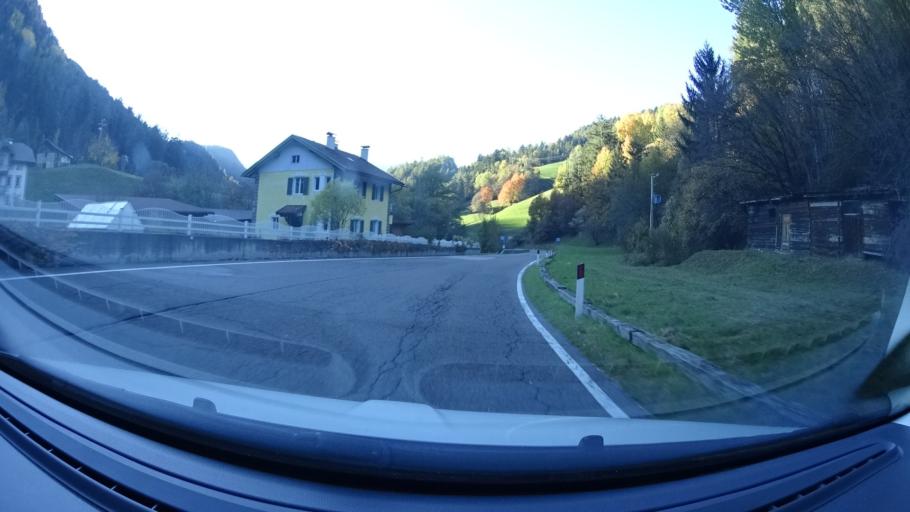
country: IT
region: Trentino-Alto Adige
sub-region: Bolzano
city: Laion
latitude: 46.5944
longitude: 11.5853
